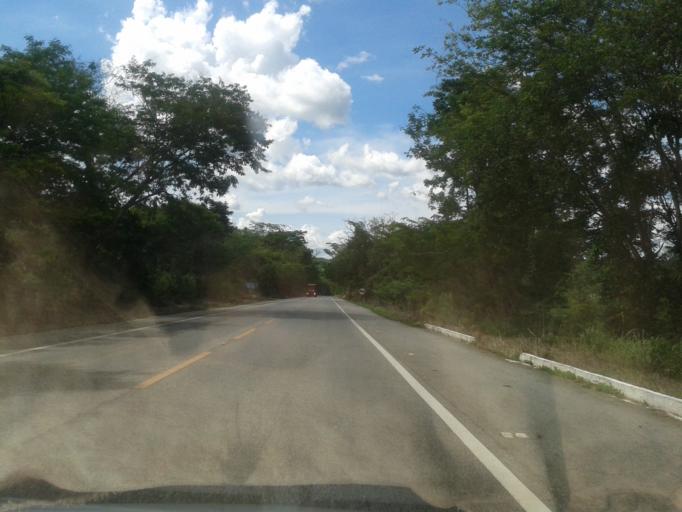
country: BR
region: Goias
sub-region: Goias
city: Goias
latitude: -15.7939
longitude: -50.1285
